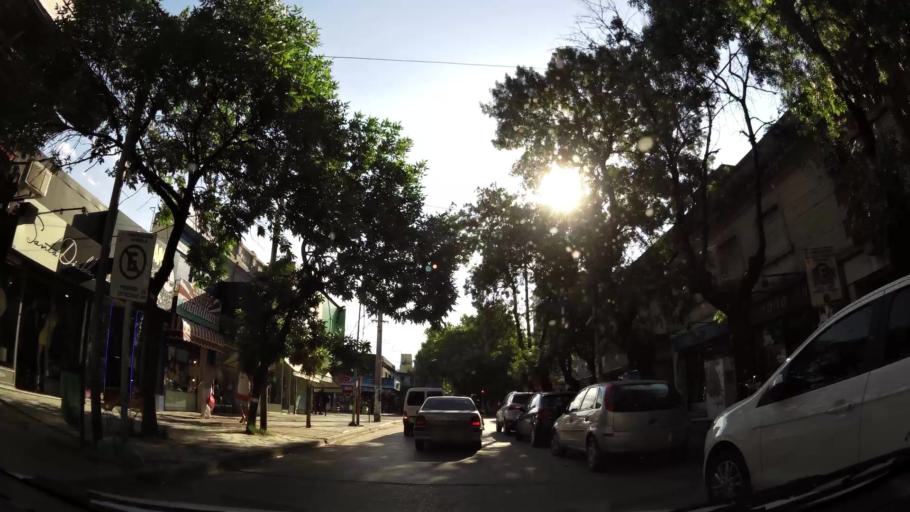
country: AR
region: Buenos Aires
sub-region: Partido de Merlo
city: Merlo
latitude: -34.6676
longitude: -58.7260
